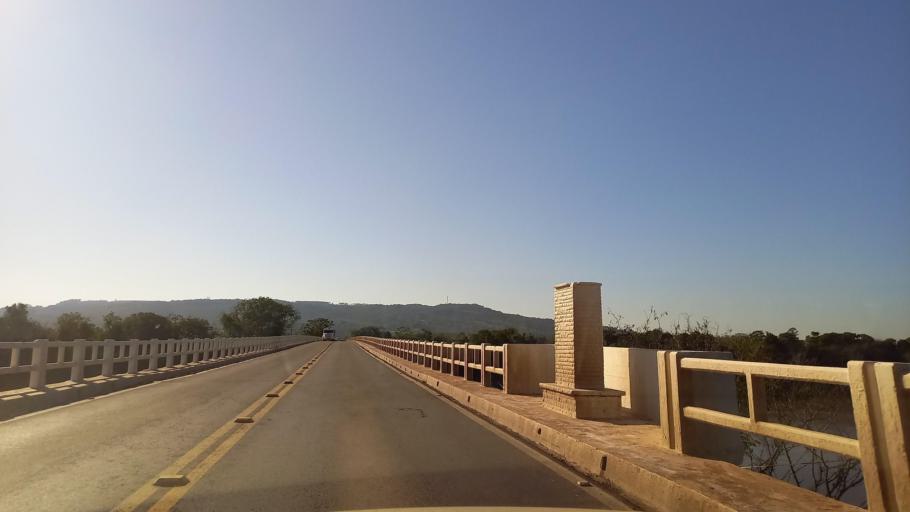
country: BR
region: Rio Grande do Sul
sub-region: Taquari
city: Taquari
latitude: -29.6874
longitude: -51.9721
